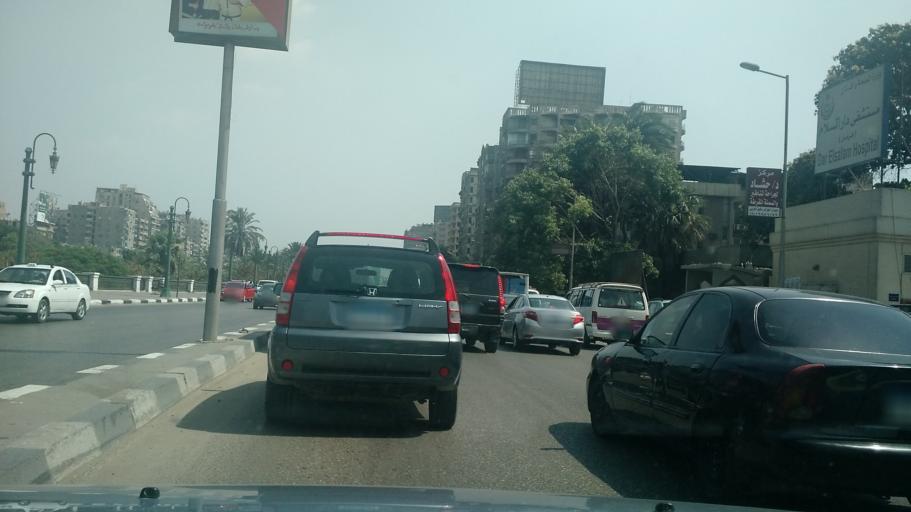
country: EG
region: Al Jizah
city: Al Jizah
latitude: 30.0126
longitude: 31.2281
